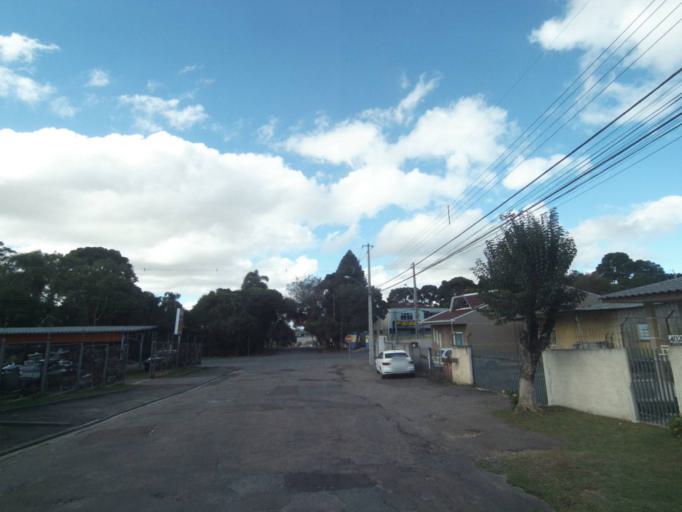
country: BR
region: Parana
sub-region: Sao Jose Dos Pinhais
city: Sao Jose dos Pinhais
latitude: -25.5298
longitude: -49.2877
